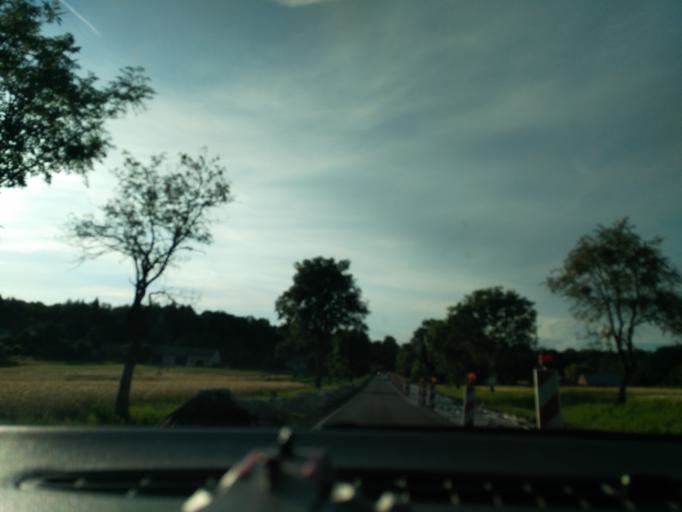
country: PL
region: Lublin Voivodeship
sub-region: Powiat krasnicki
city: Szastarka
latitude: 50.8435
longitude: 22.2955
